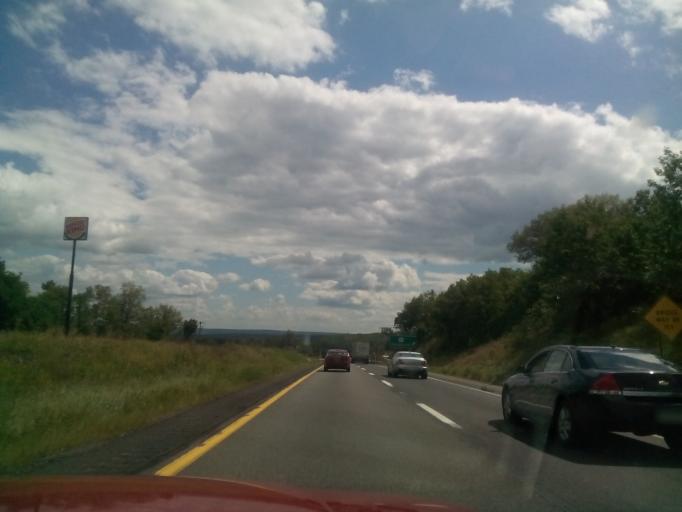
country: US
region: Pennsylvania
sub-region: Monroe County
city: Tannersville
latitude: 41.0424
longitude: -75.3136
